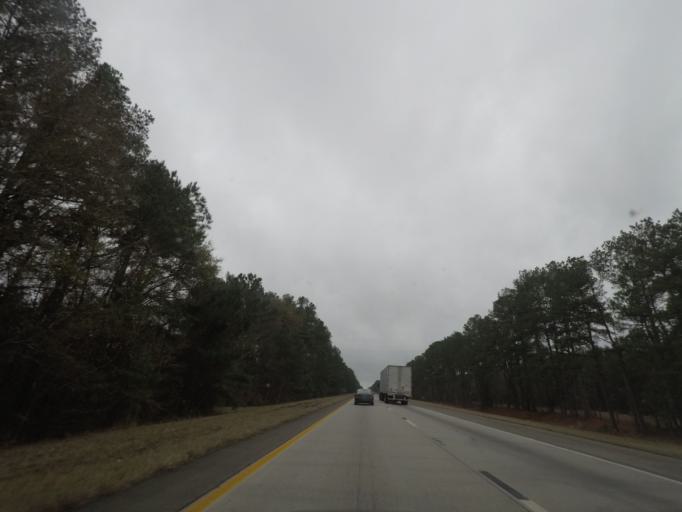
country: US
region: South Carolina
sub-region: Colleton County
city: Walterboro
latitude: 33.0109
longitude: -80.6678
